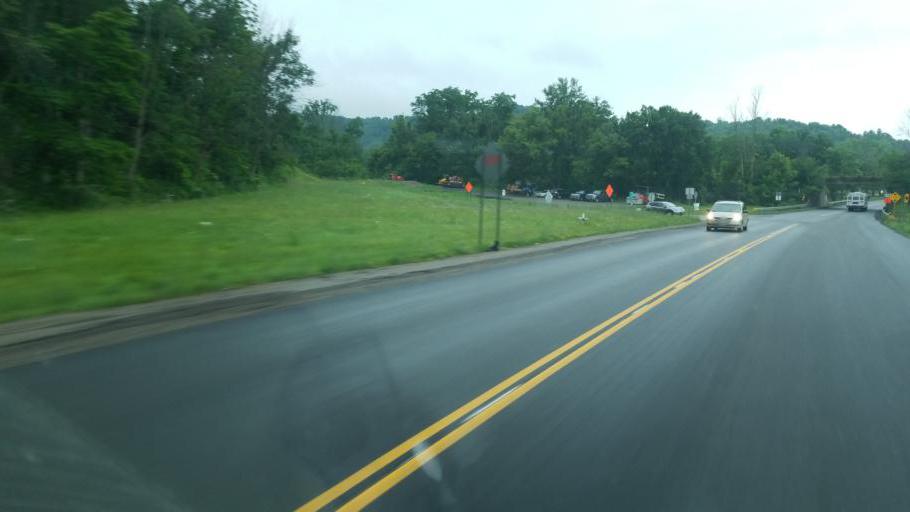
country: US
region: Ohio
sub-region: Tuscarawas County
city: Dennison
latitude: 40.3914
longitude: -81.2622
